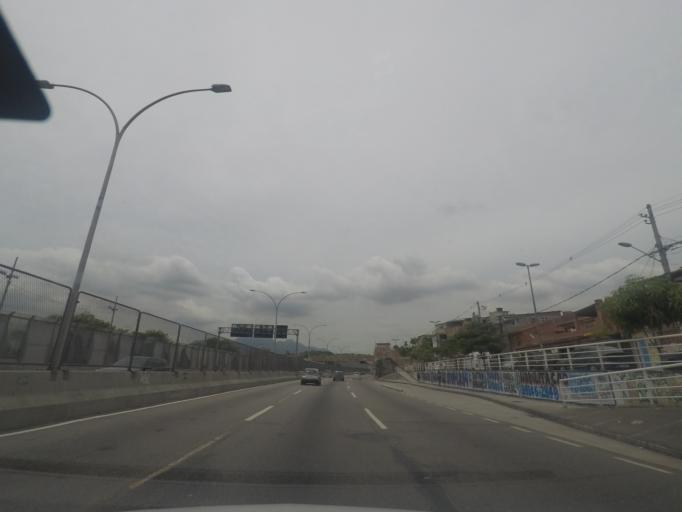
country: BR
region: Rio de Janeiro
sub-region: Rio De Janeiro
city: Rio de Janeiro
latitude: -22.8675
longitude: -43.2409
